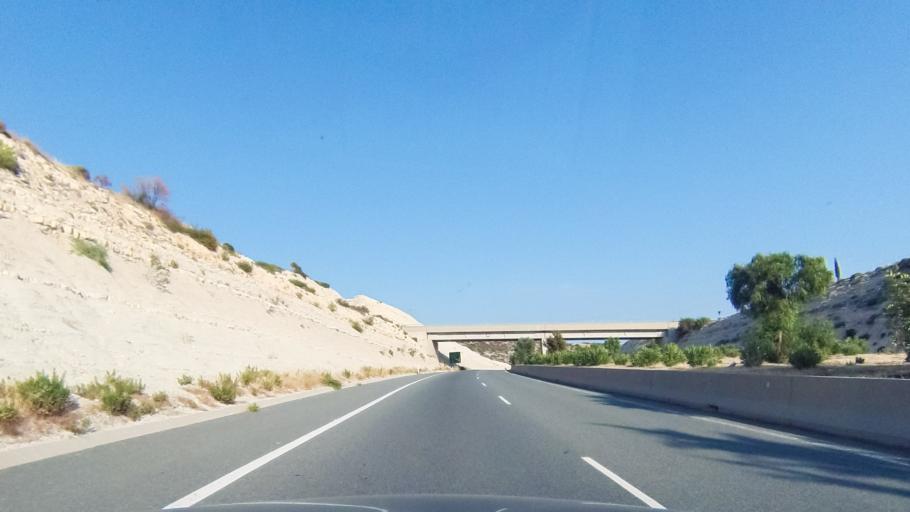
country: CY
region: Limassol
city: Sotira
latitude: 34.7025
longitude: 32.8566
